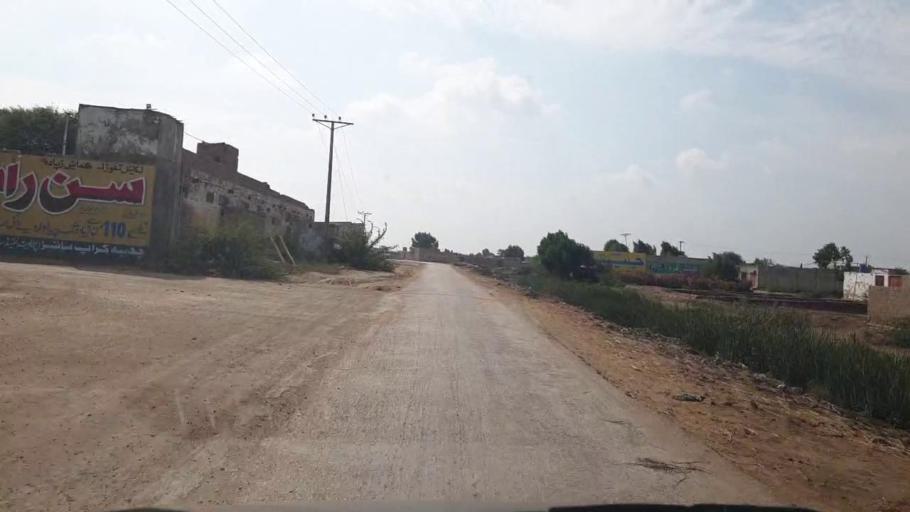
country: PK
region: Sindh
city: Kario
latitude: 24.6476
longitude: 68.5423
